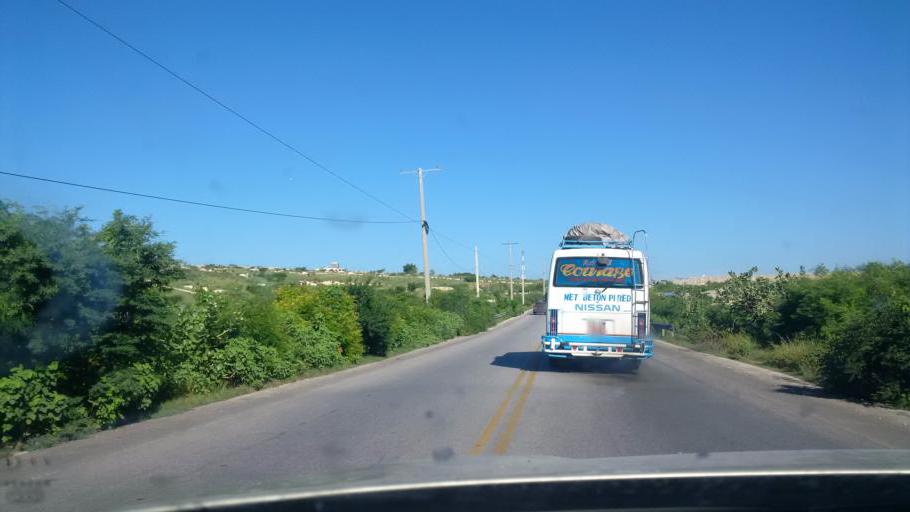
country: HT
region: Ouest
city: Cabaret
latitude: 18.7281
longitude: -72.3926
